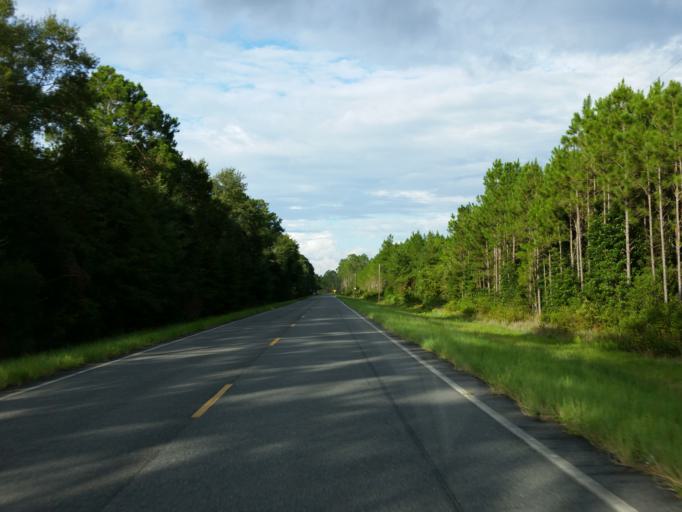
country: US
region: Florida
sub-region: Hamilton County
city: Jasper
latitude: 30.6357
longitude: -82.5876
